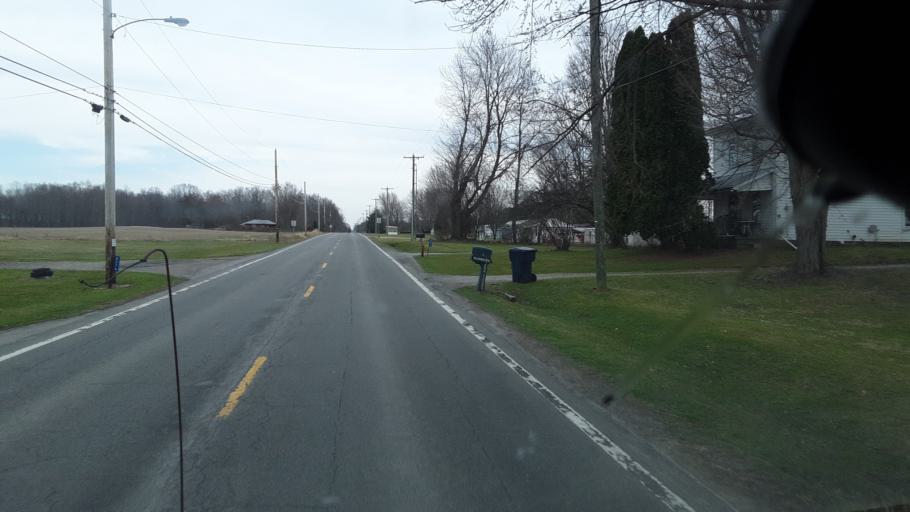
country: US
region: Ohio
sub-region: Huron County
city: Plymouth
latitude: 40.9812
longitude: -82.6676
